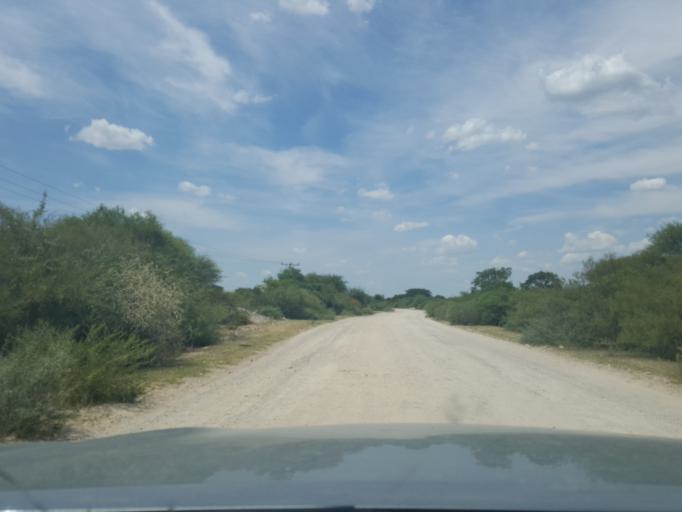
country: BW
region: North West
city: Shakawe
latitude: -18.3184
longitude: 21.9082
